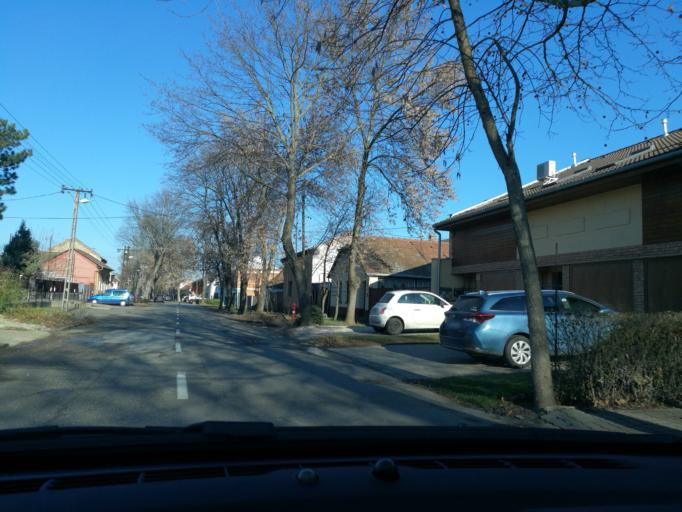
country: HU
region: Szabolcs-Szatmar-Bereg
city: Nyiregyhaza
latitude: 47.9474
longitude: 21.7250
